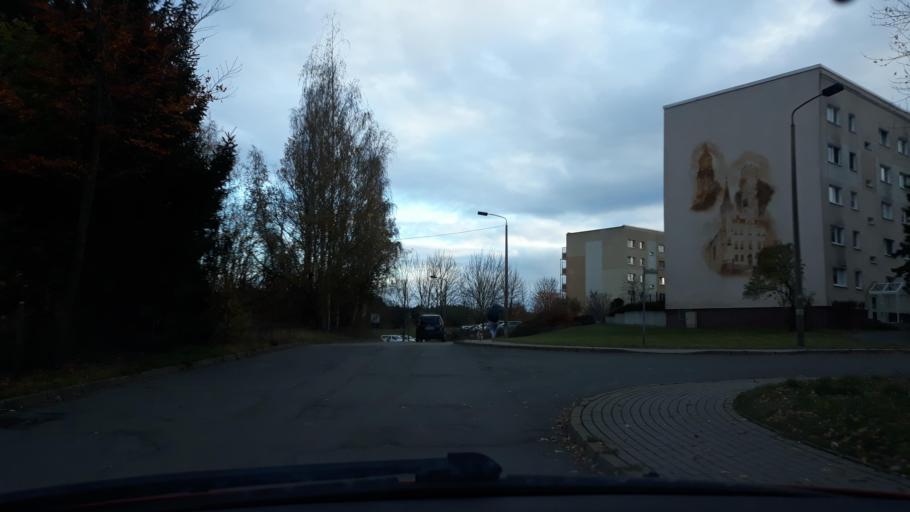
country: DE
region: Saxony
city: Kirchberg
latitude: 50.6184
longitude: 12.5179
